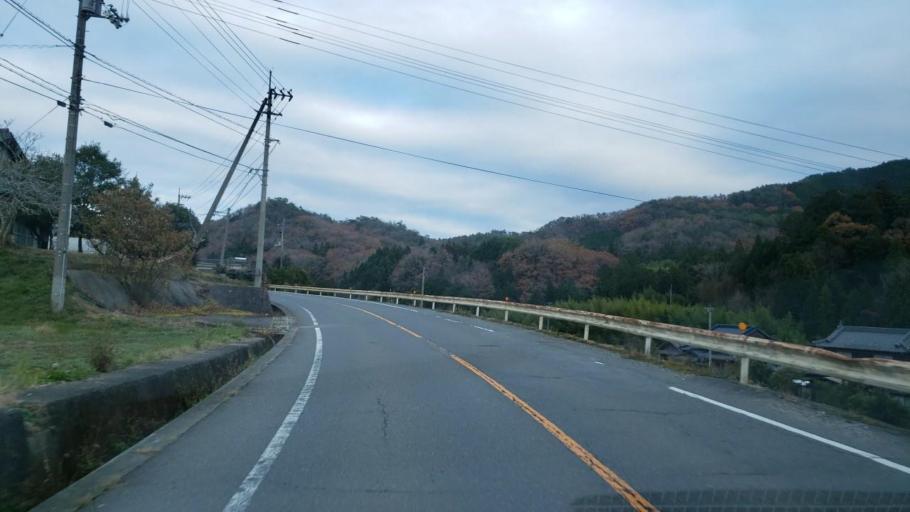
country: JP
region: Tokushima
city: Wakimachi
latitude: 34.1704
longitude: 134.1625
